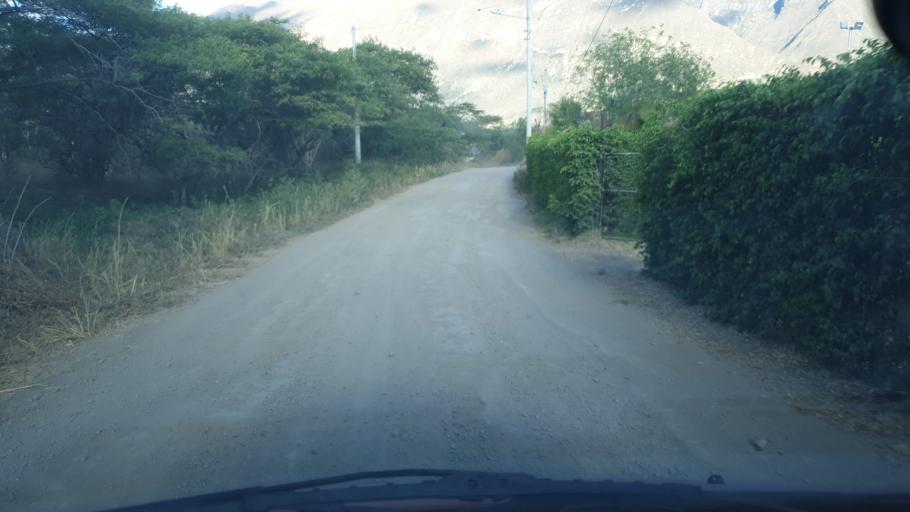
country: EC
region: Azuay
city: Cuenca
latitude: -3.2913
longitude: -79.2876
